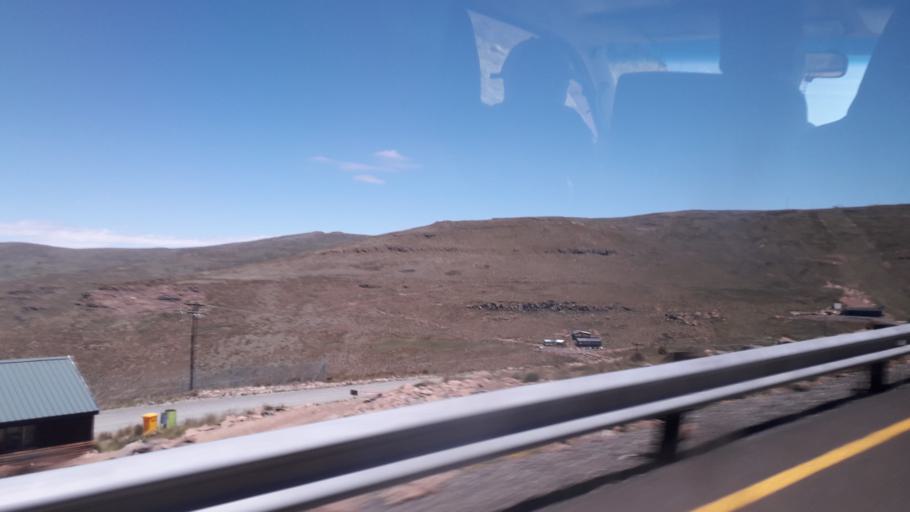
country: ZA
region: Orange Free State
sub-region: Thabo Mofutsanyana District Municipality
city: Phuthaditjhaba
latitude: -28.8288
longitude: 28.7302
